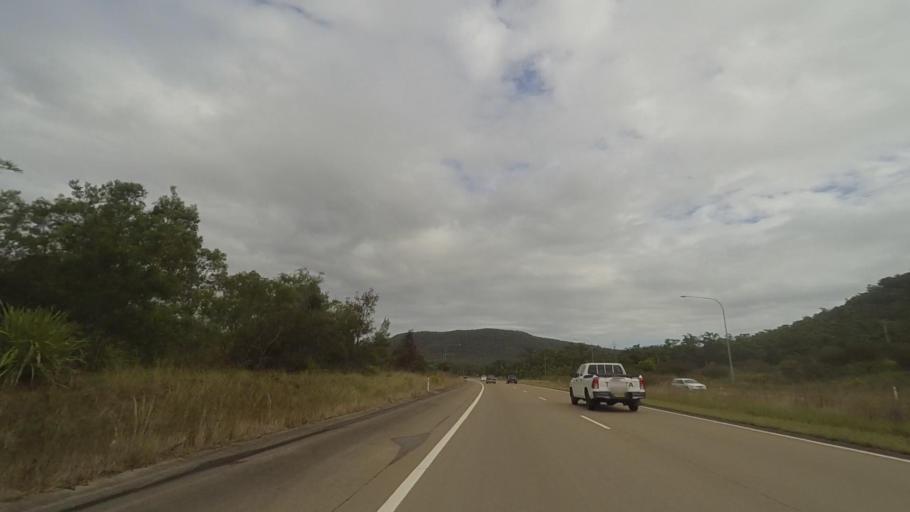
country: AU
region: New South Wales
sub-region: Port Stephens Shire
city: Port Stephens
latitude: -32.6287
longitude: 151.9907
